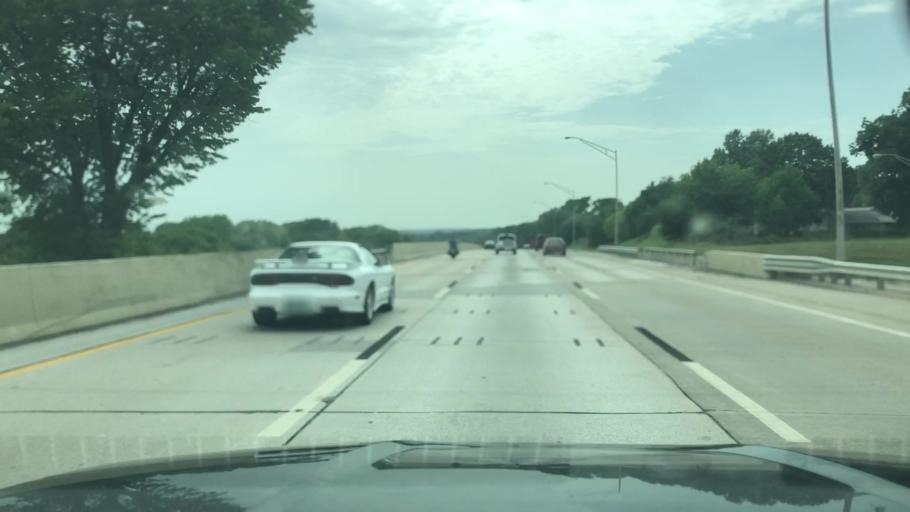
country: US
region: Oklahoma
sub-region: Tulsa County
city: Tulsa
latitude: 36.1573
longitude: -96.0291
